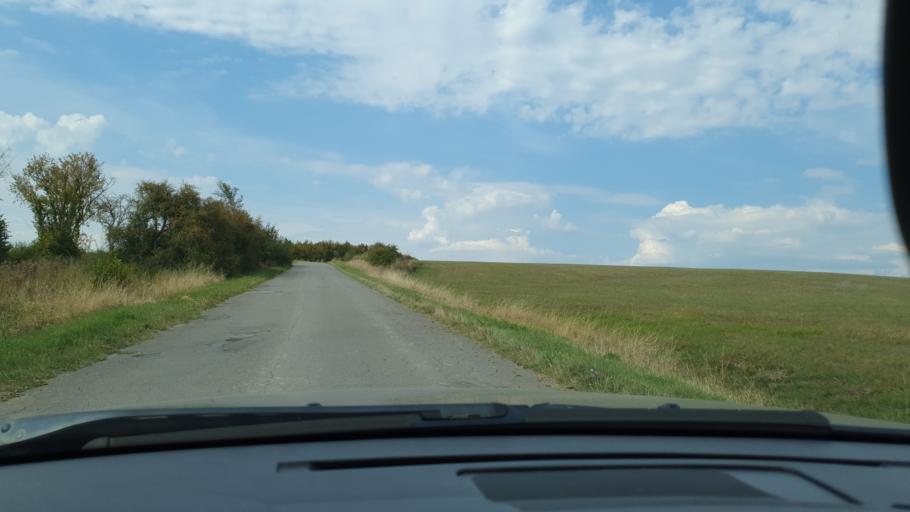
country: DE
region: Rheinland-Pfalz
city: Grossbundenbach
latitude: 49.2714
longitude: 7.3986
